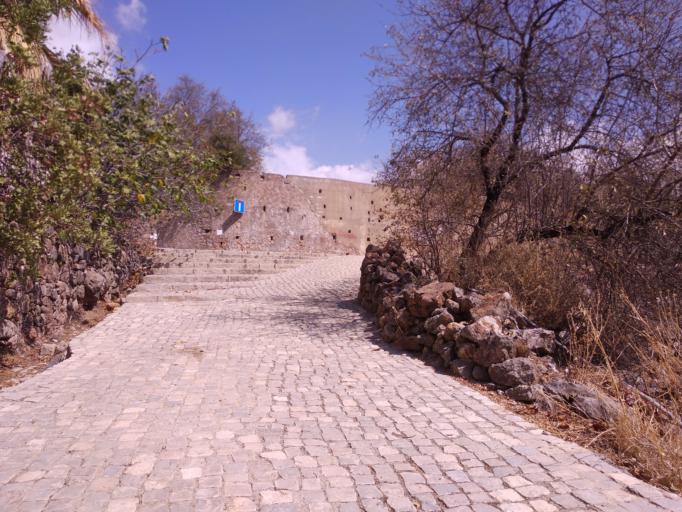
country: PT
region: Faro
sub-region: Sao Bras de Alportel
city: Sao Bras de Alportel
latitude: 37.1495
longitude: -7.8877
